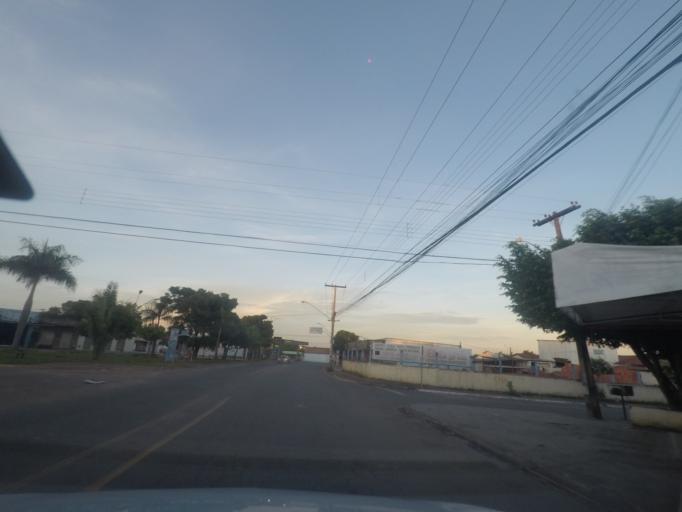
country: BR
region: Goias
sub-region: Goiania
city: Goiania
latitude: -16.6896
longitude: -49.3374
